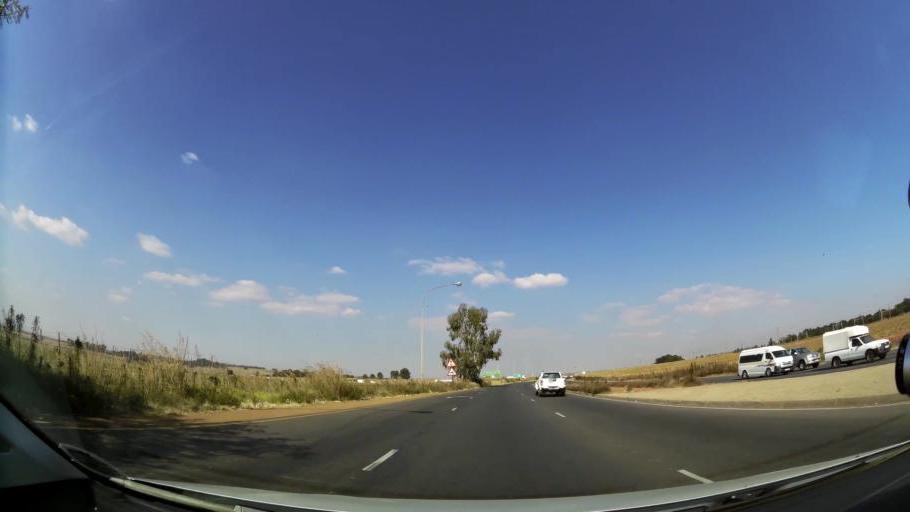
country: ZA
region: Gauteng
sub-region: Ekurhuleni Metropolitan Municipality
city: Tembisa
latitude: -26.0407
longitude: 28.2579
